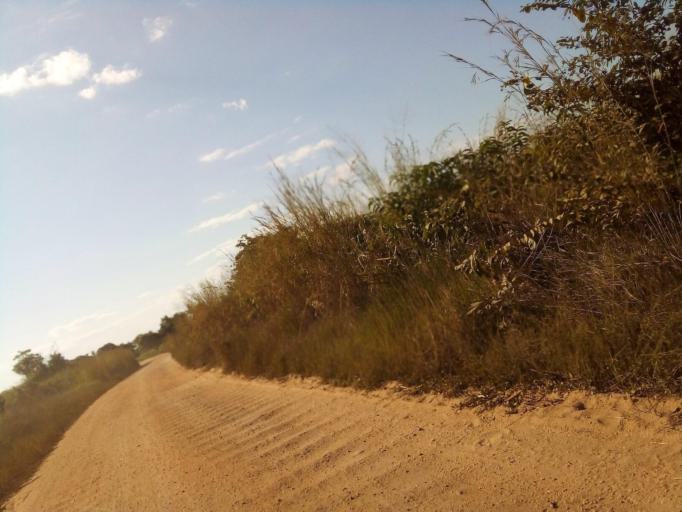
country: MZ
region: Zambezia
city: Quelimane
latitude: -17.5356
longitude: 36.6222
